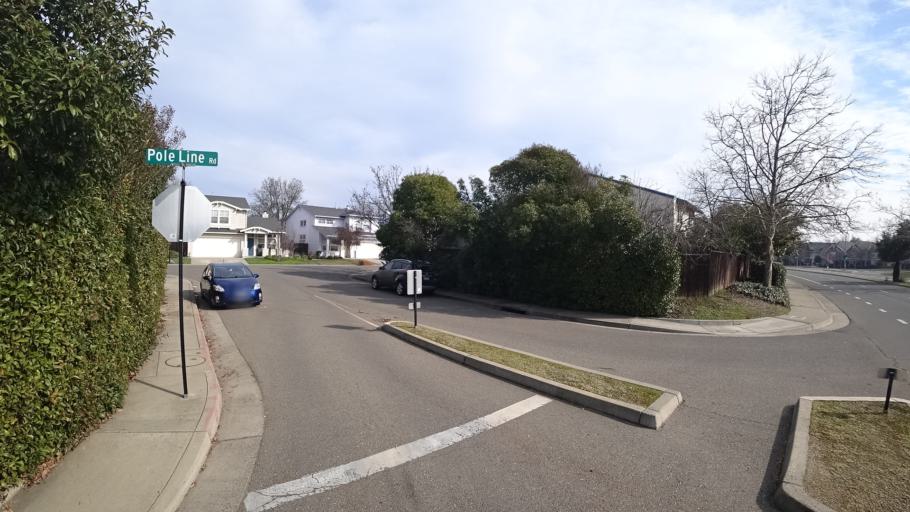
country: US
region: California
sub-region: Yolo County
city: Davis
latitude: 38.5421
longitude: -121.7242
